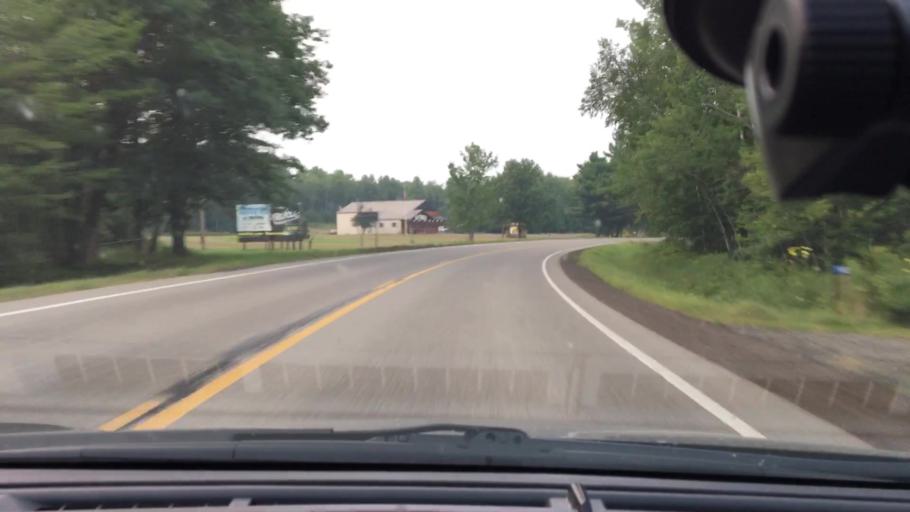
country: US
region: Minnesota
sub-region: Crow Wing County
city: Cross Lake
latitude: 46.8243
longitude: -93.9482
